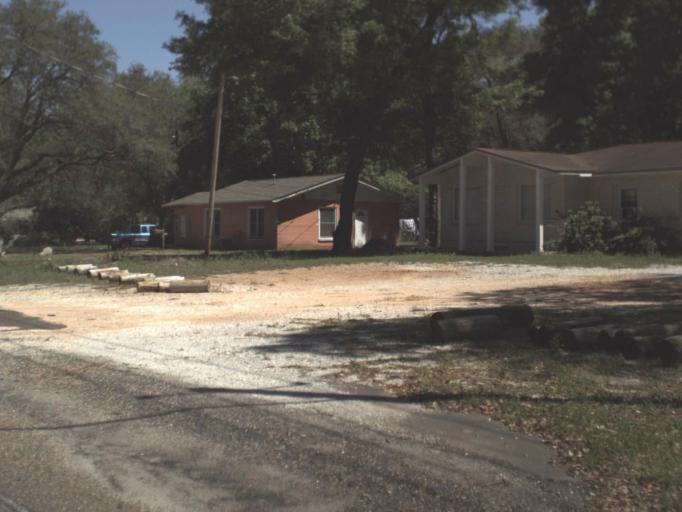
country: US
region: Florida
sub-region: Escambia County
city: Myrtle Grove
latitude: 30.4316
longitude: -87.3063
